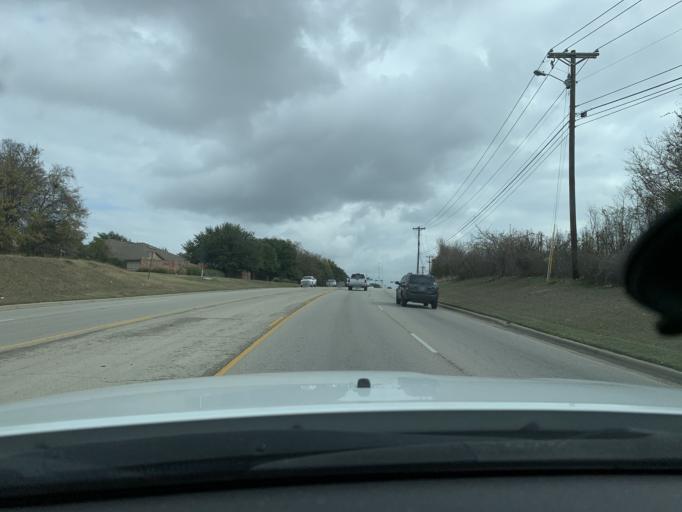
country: US
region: Texas
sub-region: Williamson County
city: Round Rock
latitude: 30.5648
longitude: -97.6725
